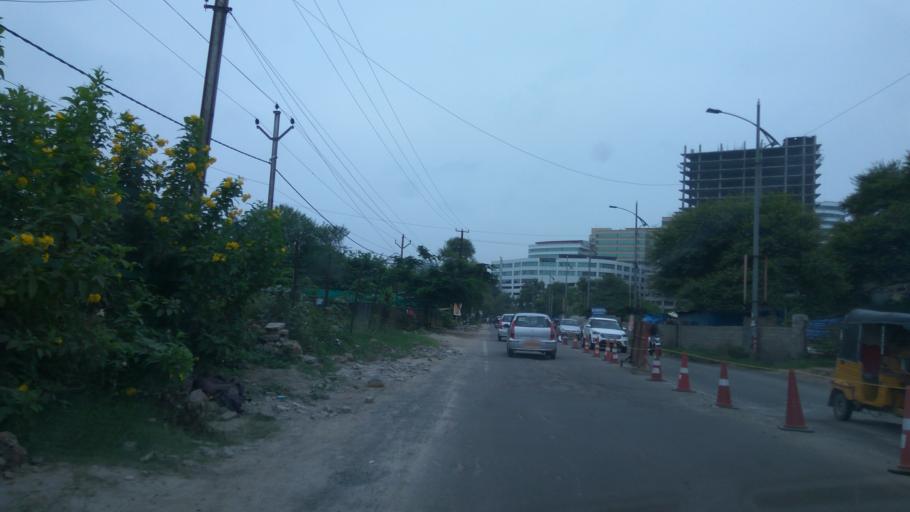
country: IN
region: Telangana
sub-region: Rangareddi
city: Kukatpalli
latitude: 17.4358
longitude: 78.3884
